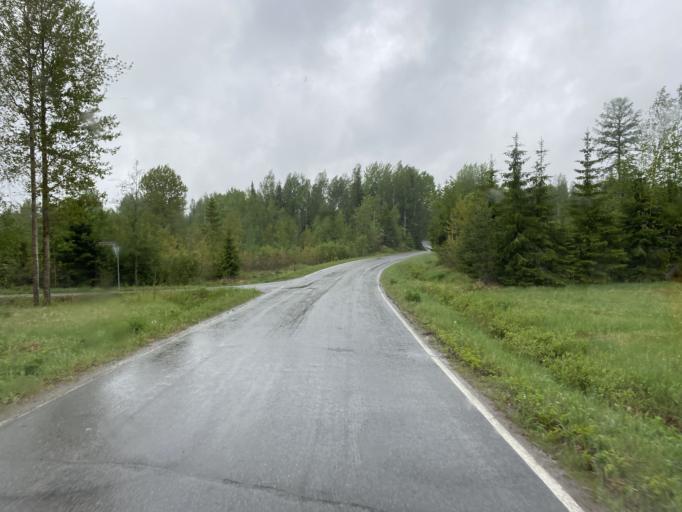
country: FI
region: Haeme
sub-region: Forssa
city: Humppila
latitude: 61.0794
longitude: 23.3115
